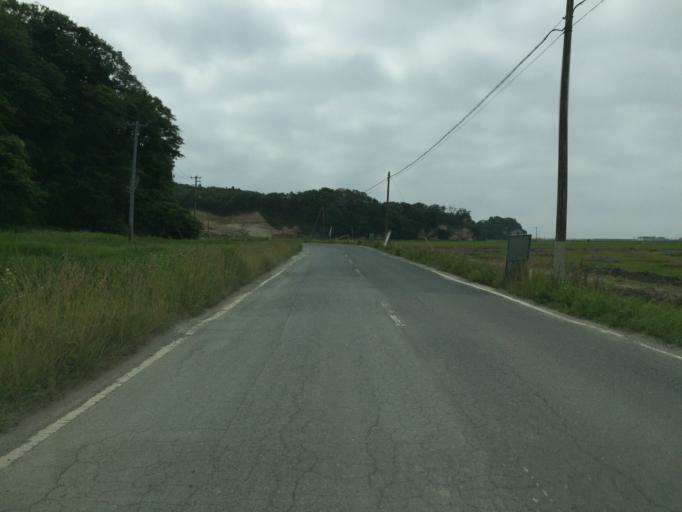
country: JP
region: Fukushima
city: Namie
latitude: 37.7357
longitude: 140.9946
